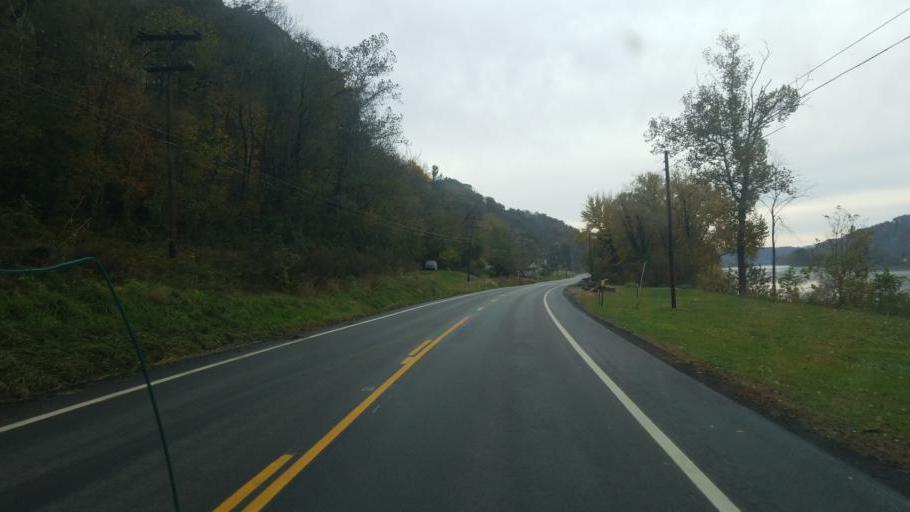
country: US
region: Ohio
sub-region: Washington County
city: Beverly
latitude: 39.5649
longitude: -81.5732
